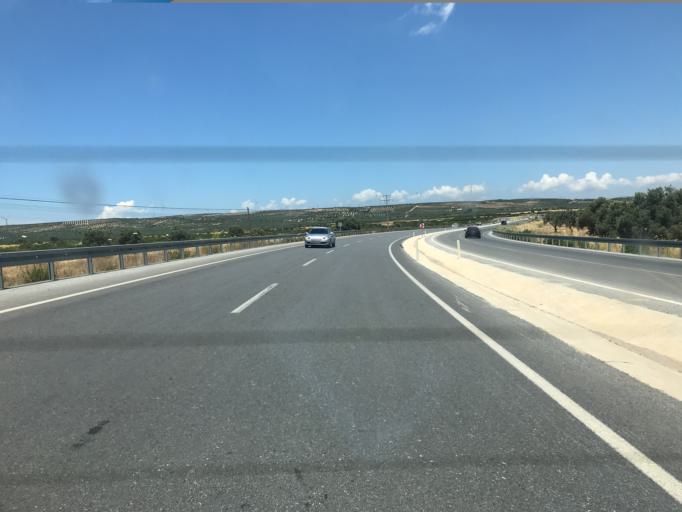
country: TR
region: Aydin
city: Akkoy
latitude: 37.4579
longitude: 27.3403
